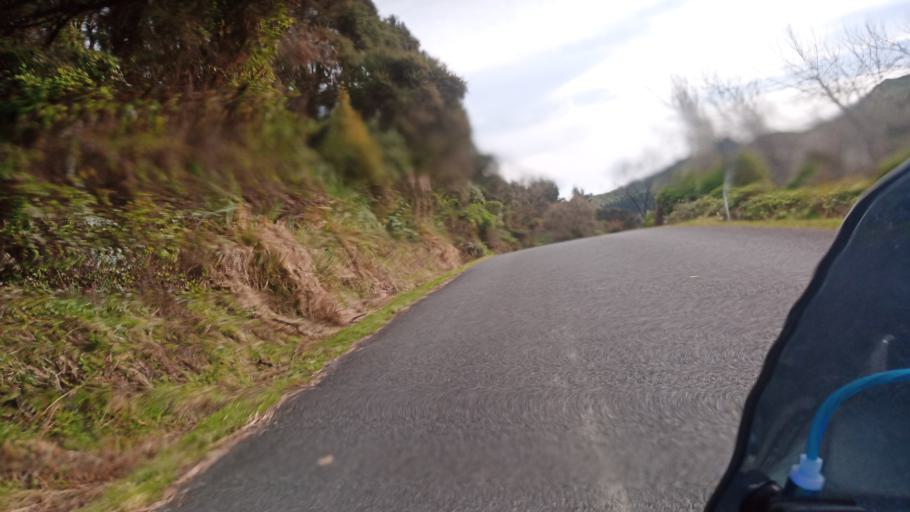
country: NZ
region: Hawke's Bay
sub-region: Wairoa District
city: Wairoa
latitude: -38.8293
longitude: 177.5171
